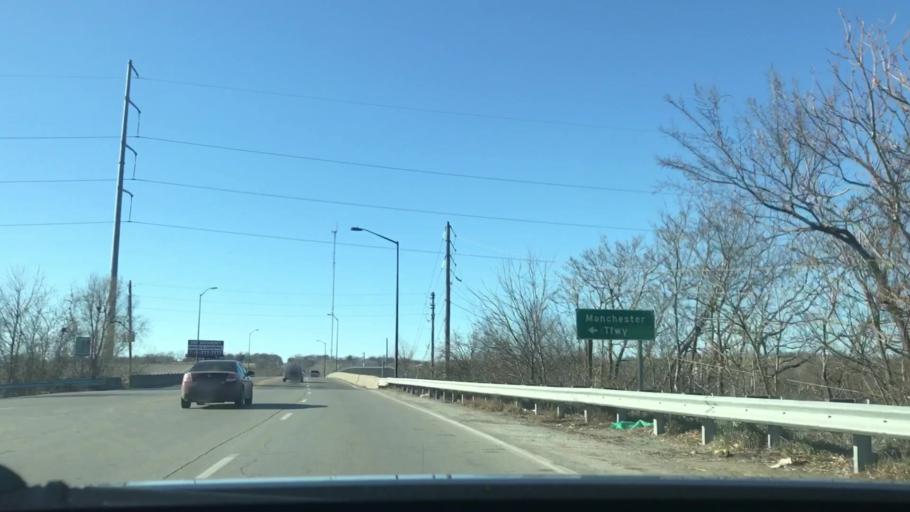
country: US
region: Missouri
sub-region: Jackson County
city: Sugar Creek
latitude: 39.0825
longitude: -94.4918
